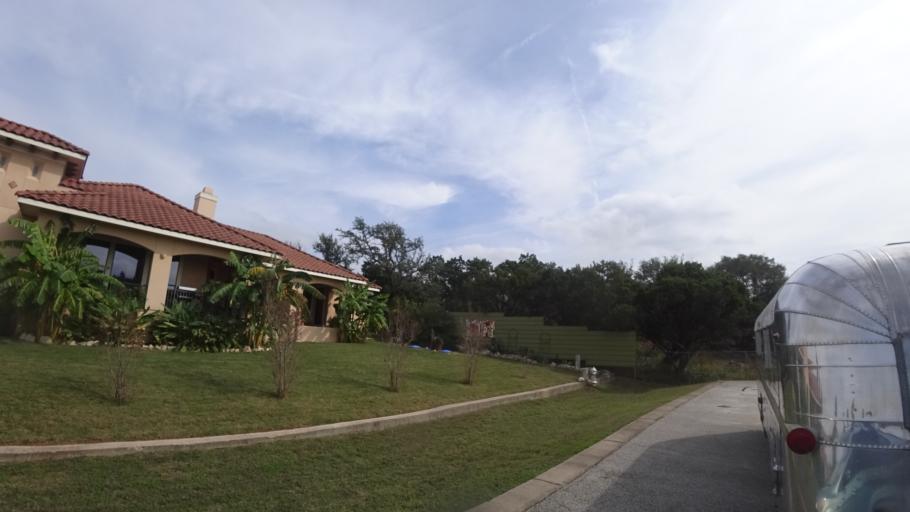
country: US
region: Texas
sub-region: Travis County
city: Hudson Bend
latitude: 30.3858
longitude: -97.9298
